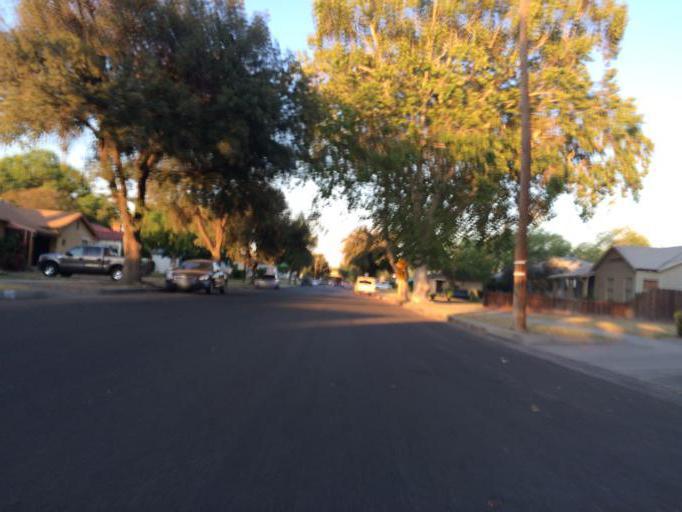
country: US
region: California
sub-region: Fresno County
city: Fresno
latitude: 36.7759
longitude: -119.7892
